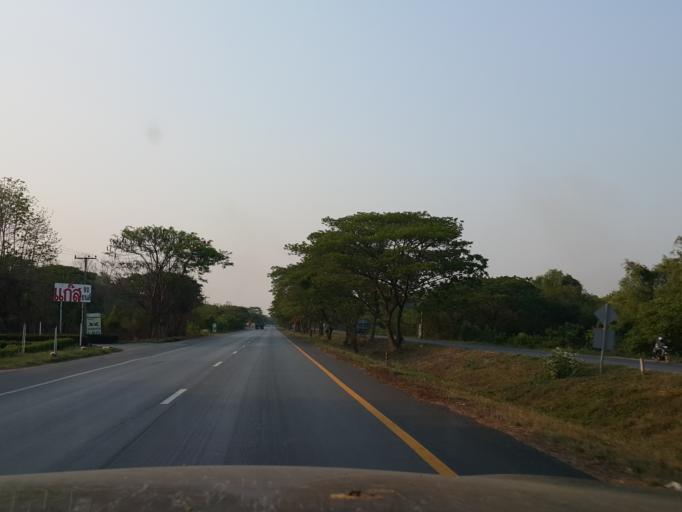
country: TH
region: Lampang
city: Sop Prap
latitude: 17.9019
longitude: 99.3412
